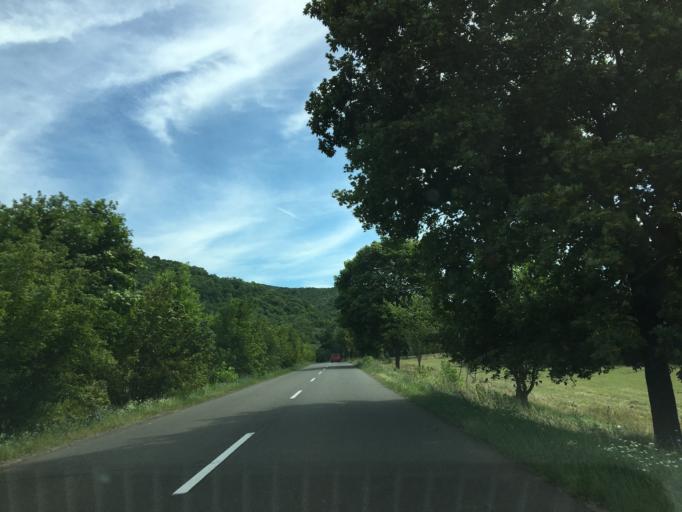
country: HU
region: Pest
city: Szob
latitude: 47.8569
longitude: 18.8099
